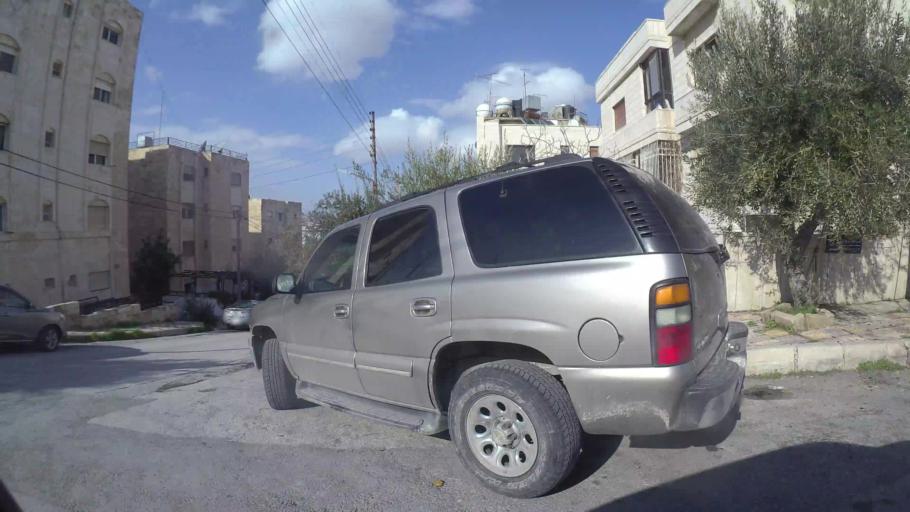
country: JO
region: Amman
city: Al Jubayhah
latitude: 32.0228
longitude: 35.8578
